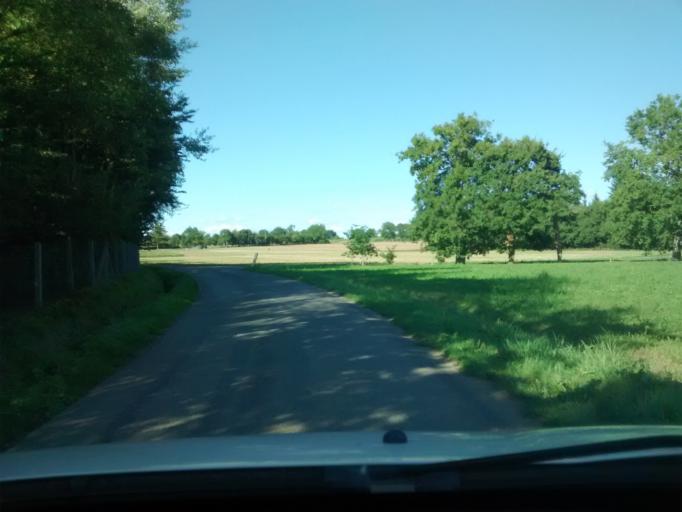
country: FR
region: Brittany
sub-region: Departement d'Ille-et-Vilaine
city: Nouvoitou
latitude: 48.0777
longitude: -1.5611
